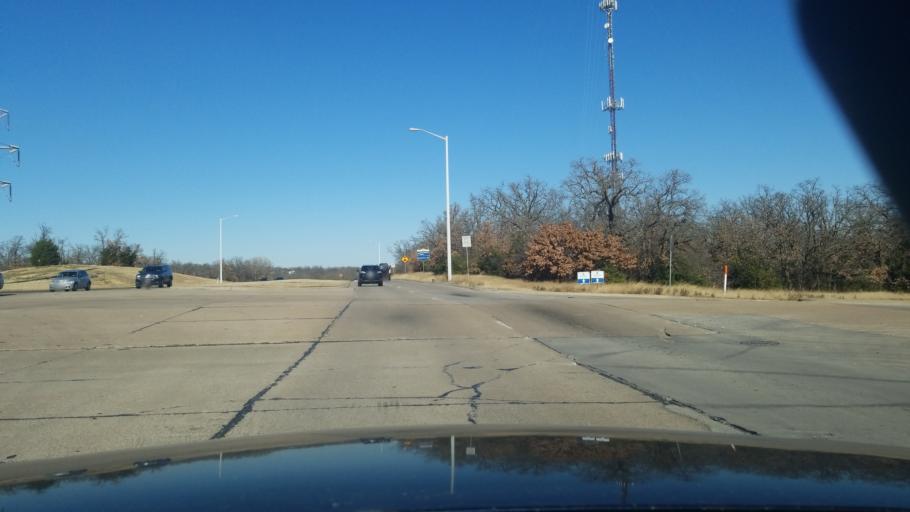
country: US
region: Texas
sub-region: Denton County
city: Corinth
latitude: 33.1772
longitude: -97.0882
